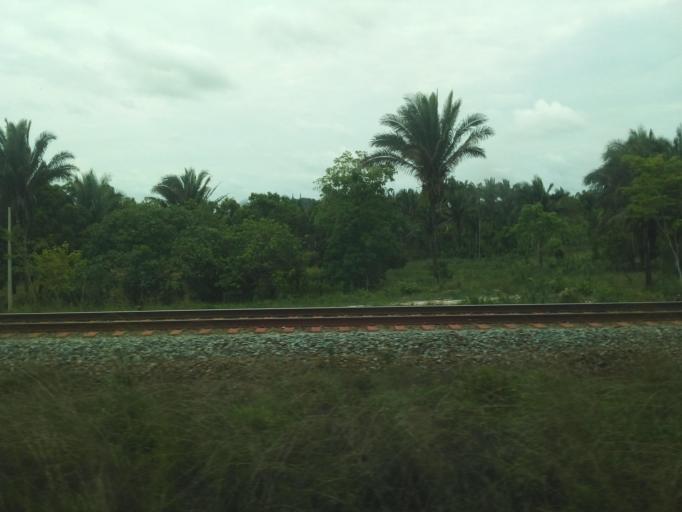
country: BR
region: Maranhao
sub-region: Santa Ines
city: Santa Ines
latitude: -3.7084
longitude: -46.0190
